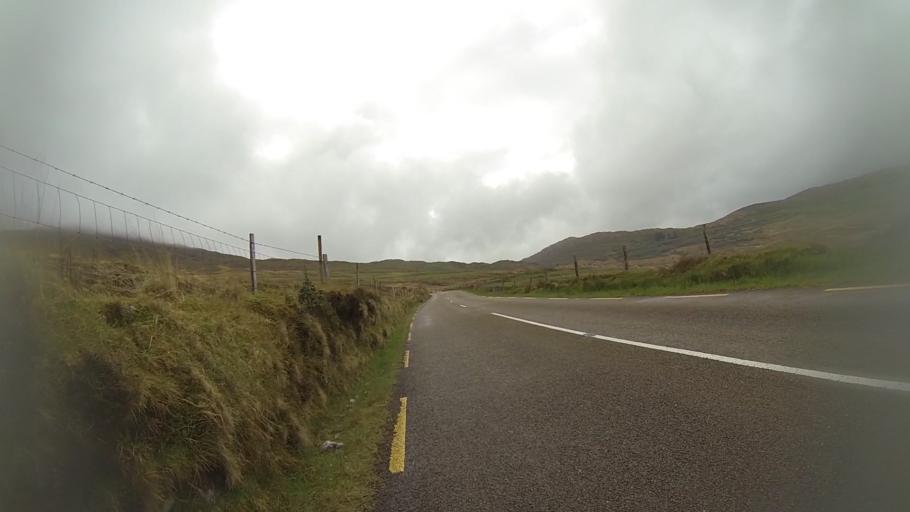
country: IE
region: Munster
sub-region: Ciarrai
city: Kenmare
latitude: 51.8789
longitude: -9.8006
